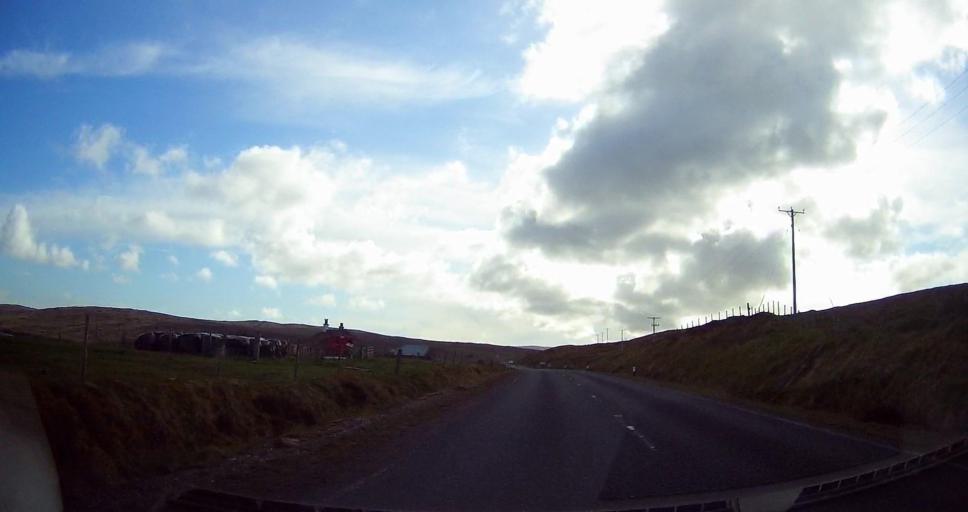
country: GB
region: Scotland
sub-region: Shetland Islands
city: Lerwick
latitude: 60.3549
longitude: -1.1693
